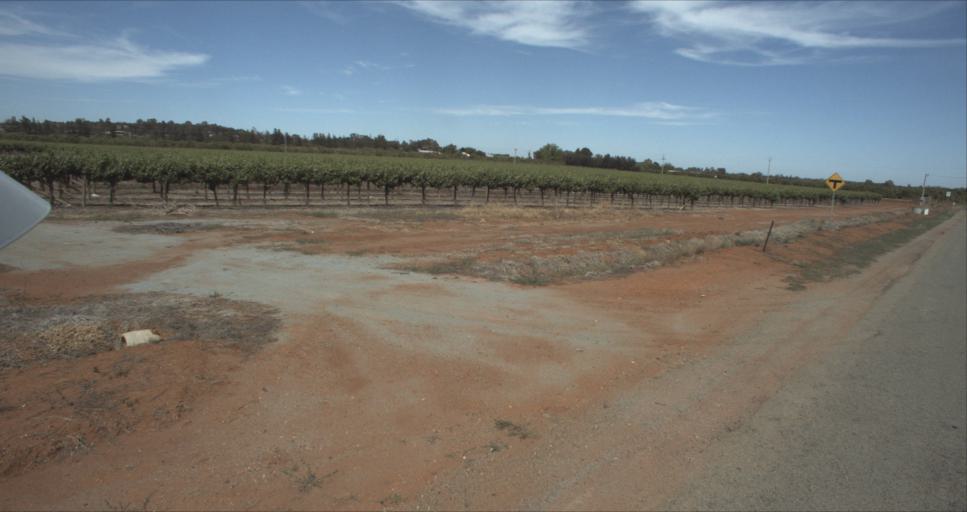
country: AU
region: New South Wales
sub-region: Leeton
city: Leeton
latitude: -34.5655
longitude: 146.4538
